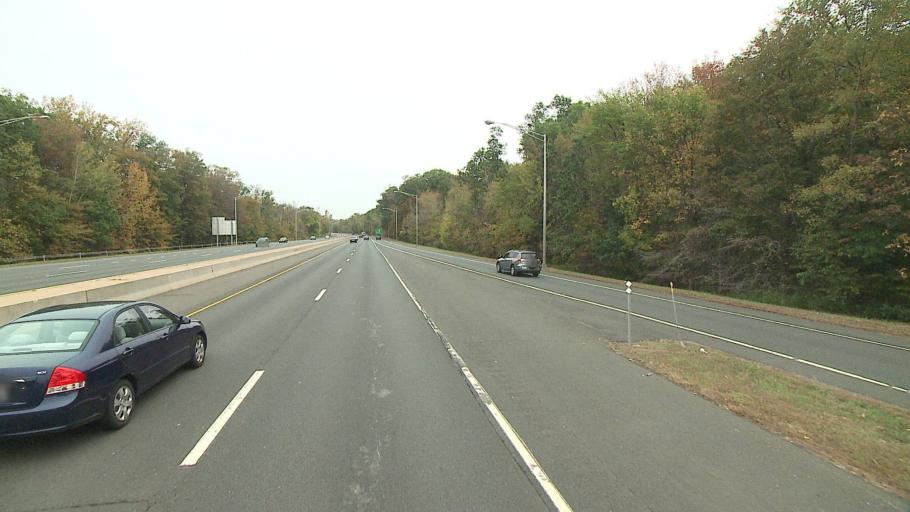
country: US
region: Connecticut
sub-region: Hartford County
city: Newington
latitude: 41.7024
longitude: -72.7577
